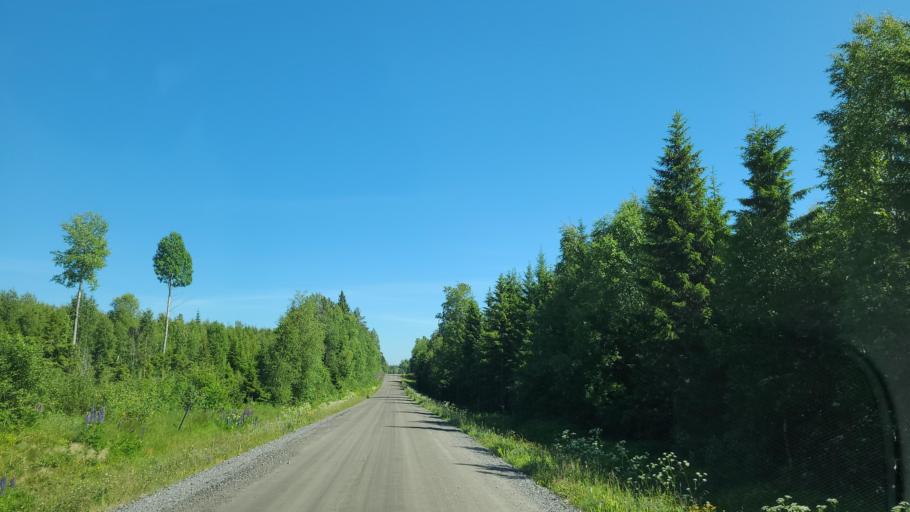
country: SE
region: Vaesterbotten
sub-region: Bjurholms Kommun
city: Bjurholm
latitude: 63.6424
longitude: 19.1263
